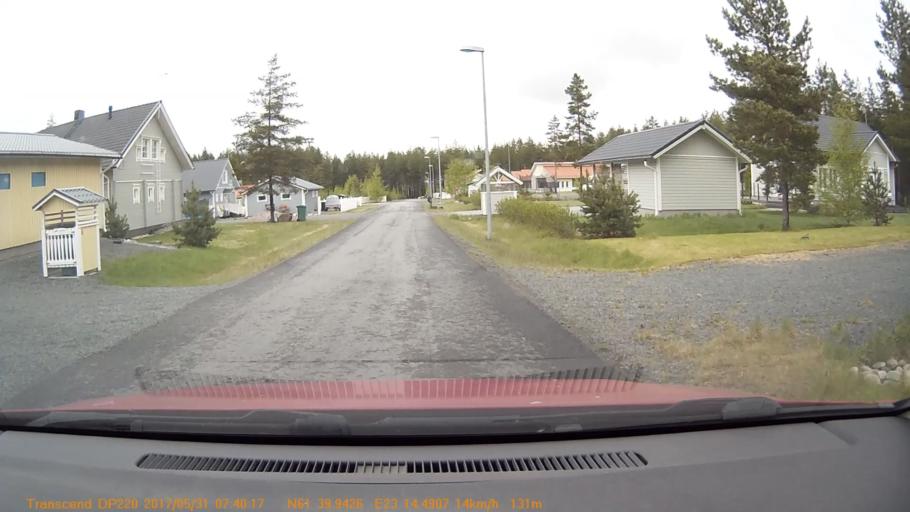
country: FI
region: Pirkanmaa
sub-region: Tampere
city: Viljakkala
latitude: 61.6657
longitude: 23.2415
